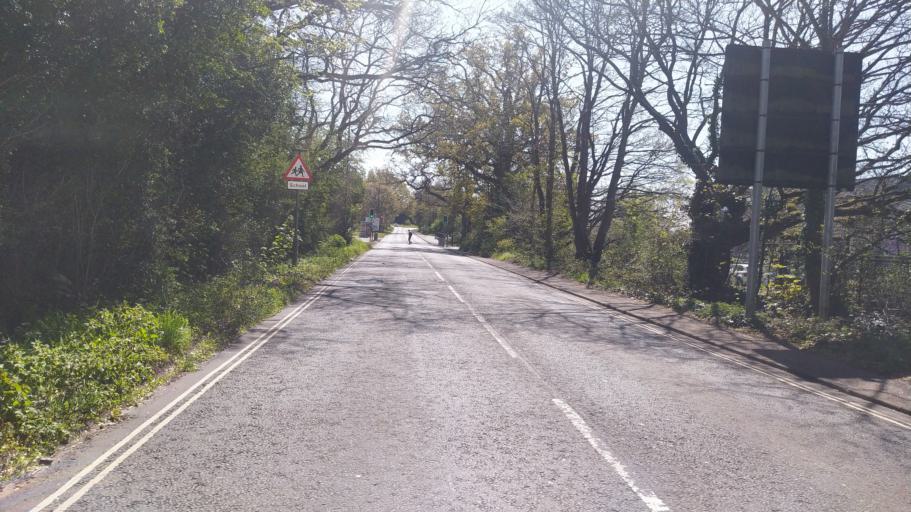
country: GB
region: England
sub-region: Hampshire
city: Totton
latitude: 50.9421
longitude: -1.4584
